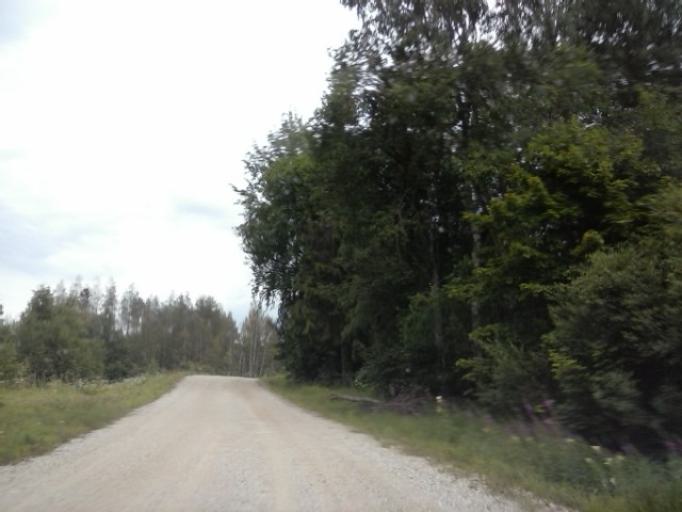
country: EE
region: Vorumaa
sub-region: Voru linn
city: Voru
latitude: 57.7417
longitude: 27.0921
